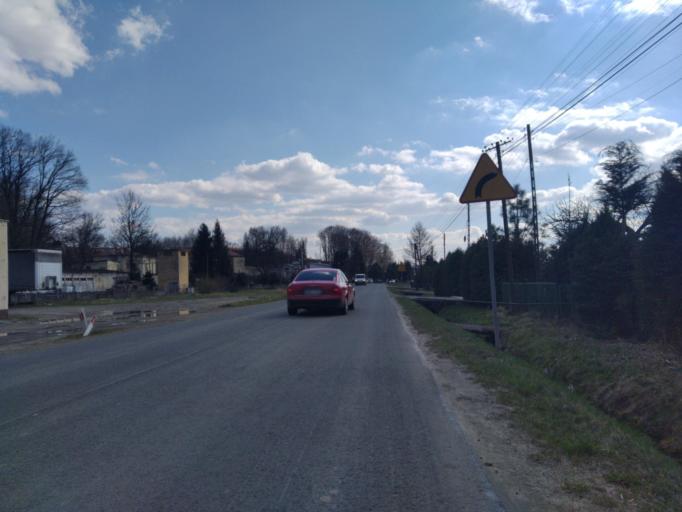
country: PL
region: Subcarpathian Voivodeship
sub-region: Powiat brzozowski
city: Grabownica Starzenska
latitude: 49.6666
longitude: 22.0830
